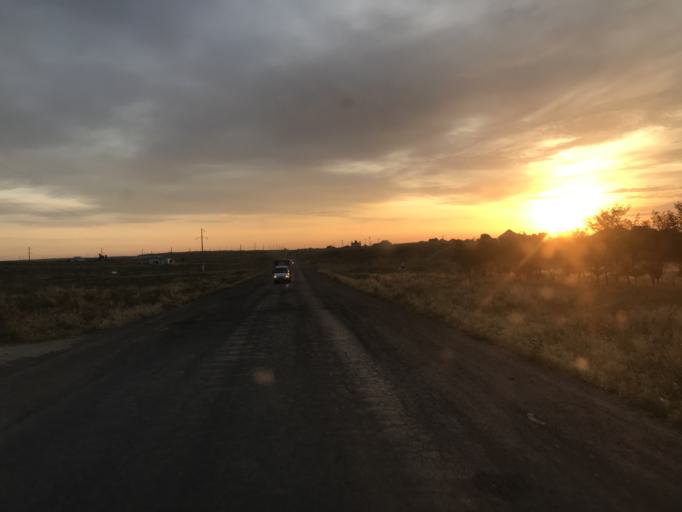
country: UZ
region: Toshkent
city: Chinoz
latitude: 41.1565
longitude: 68.7424
